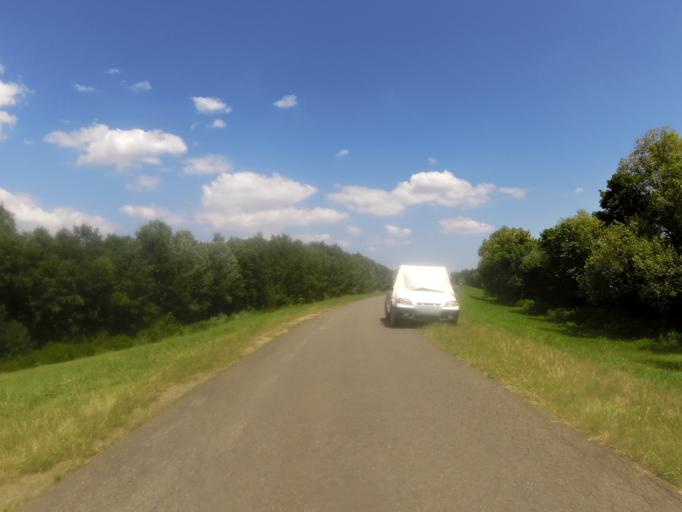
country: HU
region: Heves
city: Tiszanana
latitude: 47.5603
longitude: 20.6088
